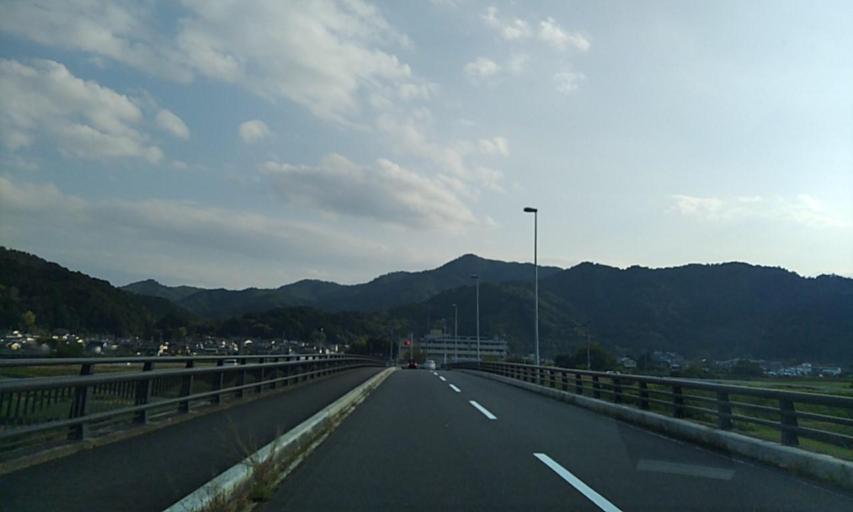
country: JP
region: Kyoto
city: Ayabe
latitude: 35.3078
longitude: 135.2047
